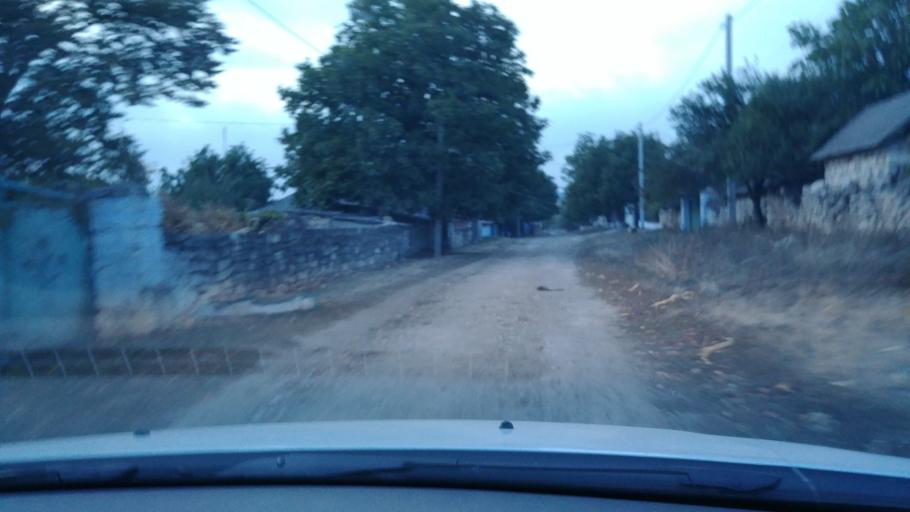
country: MD
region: Rezina
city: Saharna
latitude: 47.6776
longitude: 28.9597
